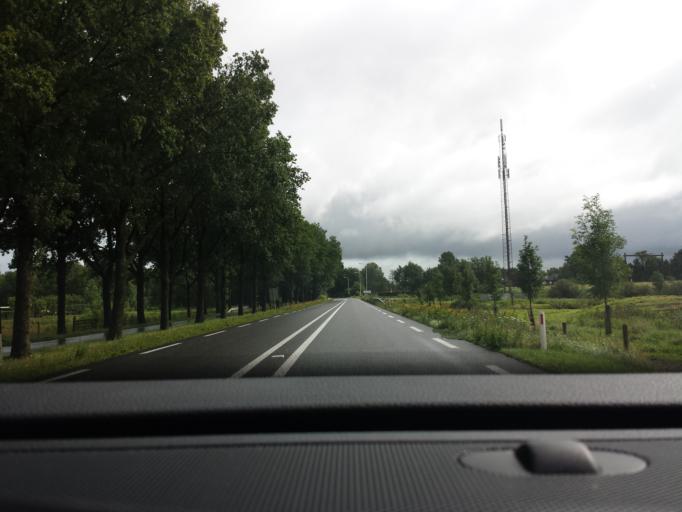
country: NL
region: Overijssel
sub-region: Gemeente Hof van Twente
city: Markelo
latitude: 52.3025
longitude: 6.4876
